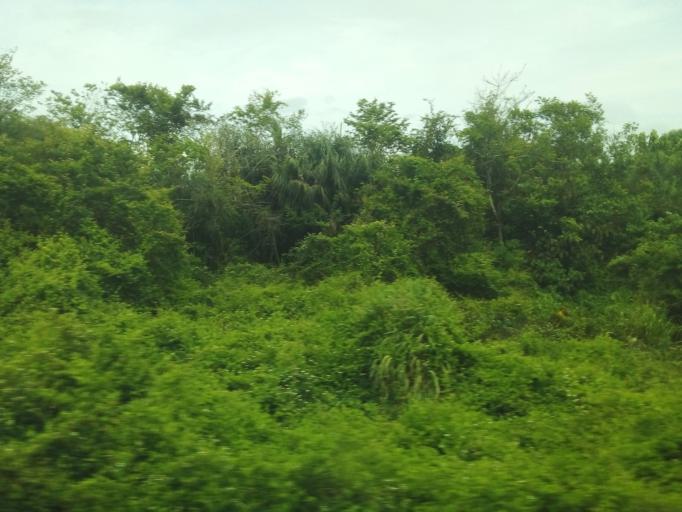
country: BR
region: Maranhao
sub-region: Anajatuba
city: Anajatuba
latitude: -3.3513
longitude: -44.5050
